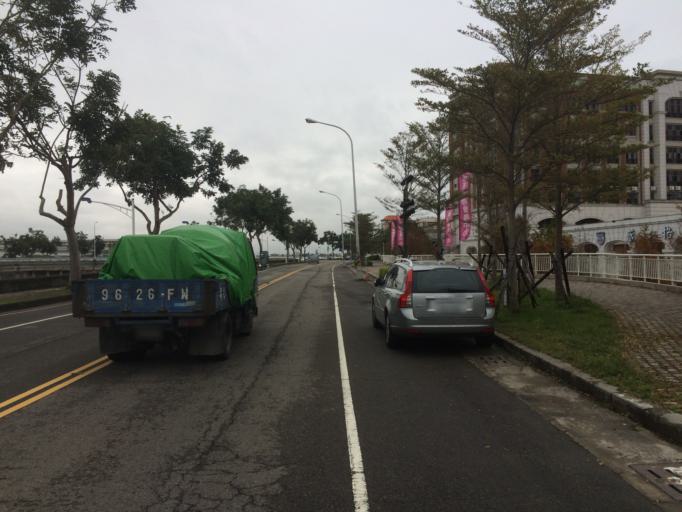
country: TW
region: Taiwan
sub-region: Taichung City
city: Taichung
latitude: 24.1786
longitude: 120.7107
